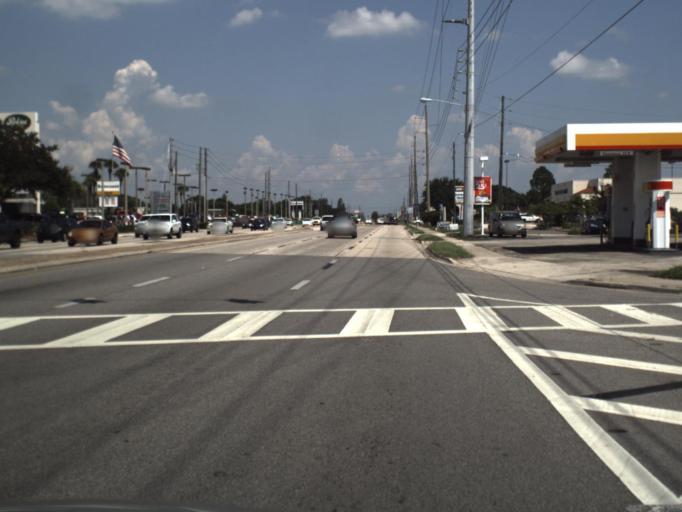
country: US
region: Florida
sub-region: Pinellas County
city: Seminole
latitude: 27.8393
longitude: -82.7621
